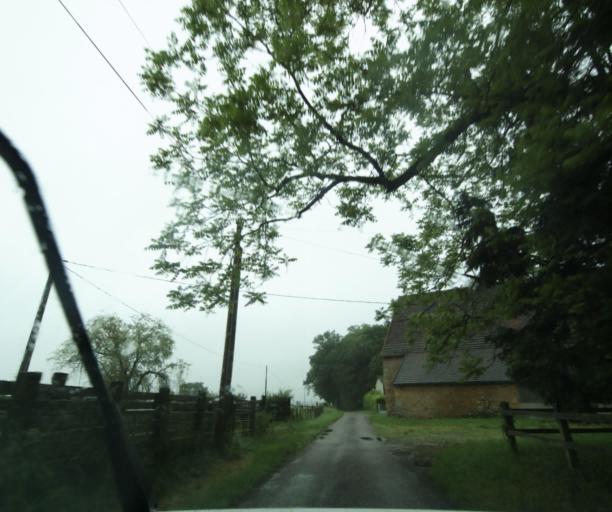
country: FR
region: Bourgogne
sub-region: Departement de Saone-et-Loire
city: Charolles
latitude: 46.4141
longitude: 4.2109
